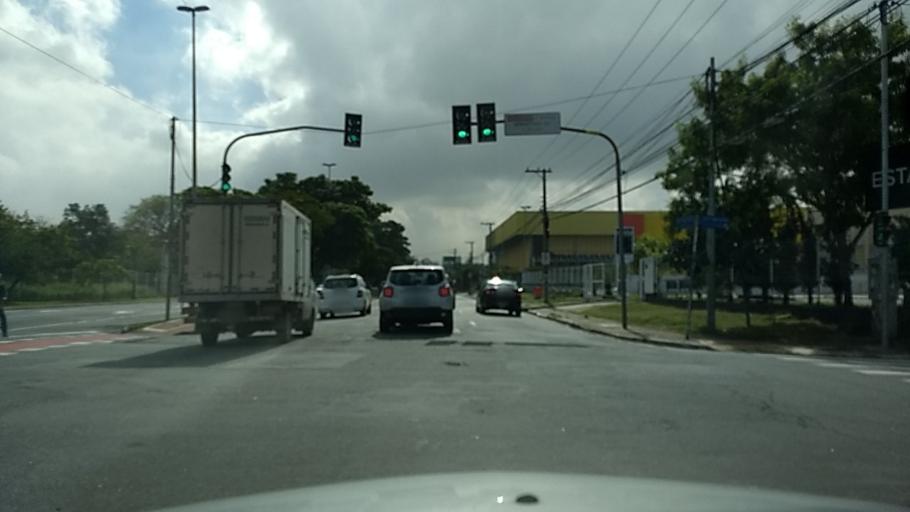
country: BR
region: Sao Paulo
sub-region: Sao Paulo
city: Sao Paulo
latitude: -23.5110
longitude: -46.6157
